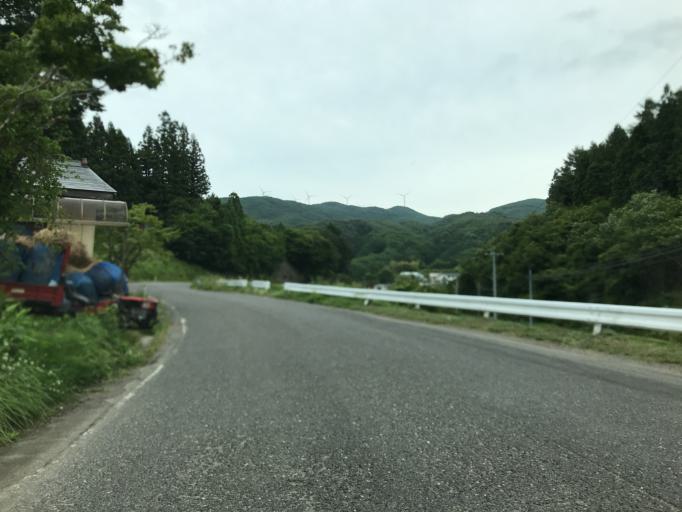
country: JP
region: Fukushima
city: Funehikimachi-funehiki
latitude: 37.3972
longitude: 140.6888
